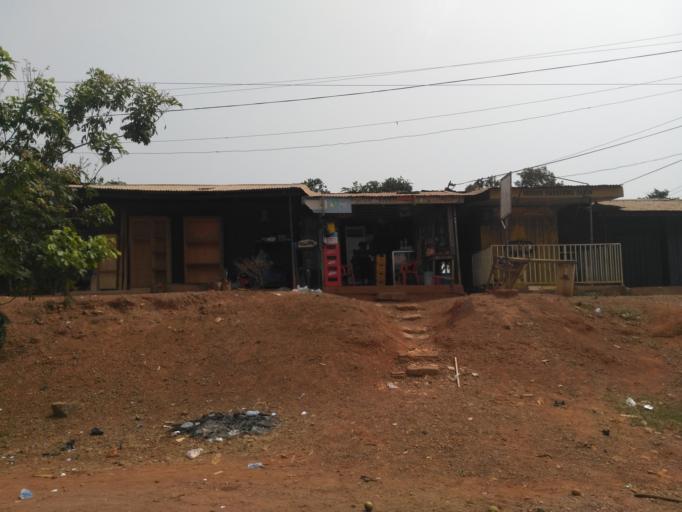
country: GH
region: Ashanti
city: Kumasi
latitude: 6.6418
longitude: -1.6451
